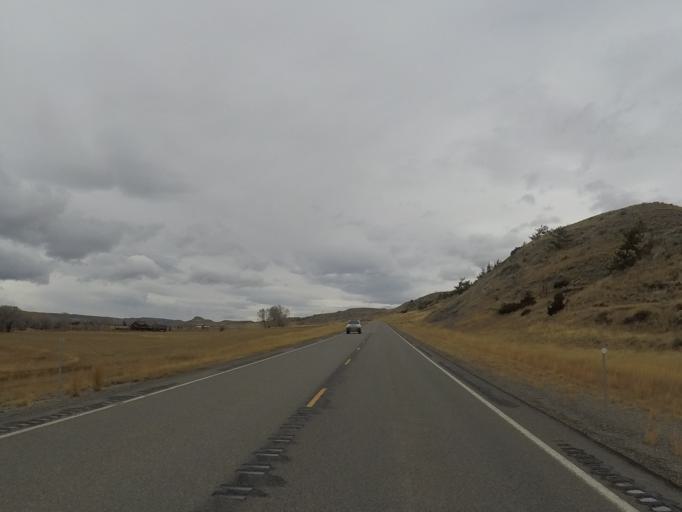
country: US
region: Montana
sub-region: Sweet Grass County
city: Big Timber
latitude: 45.9111
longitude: -109.9780
